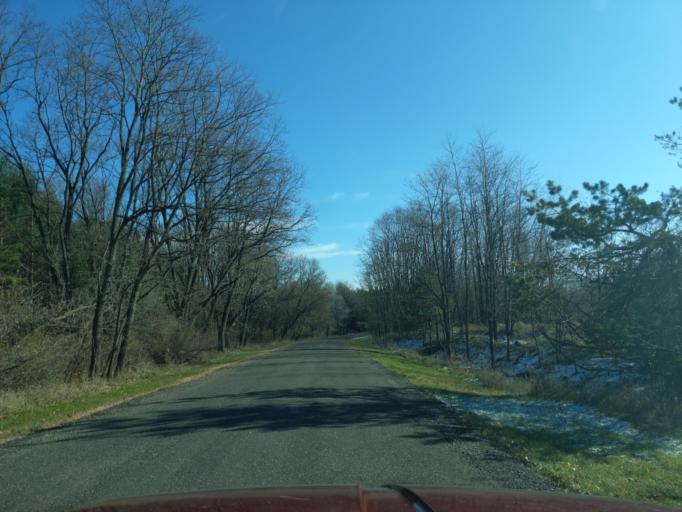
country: US
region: Wisconsin
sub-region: Waushara County
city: Silver Lake
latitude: 44.1213
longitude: -89.1783
